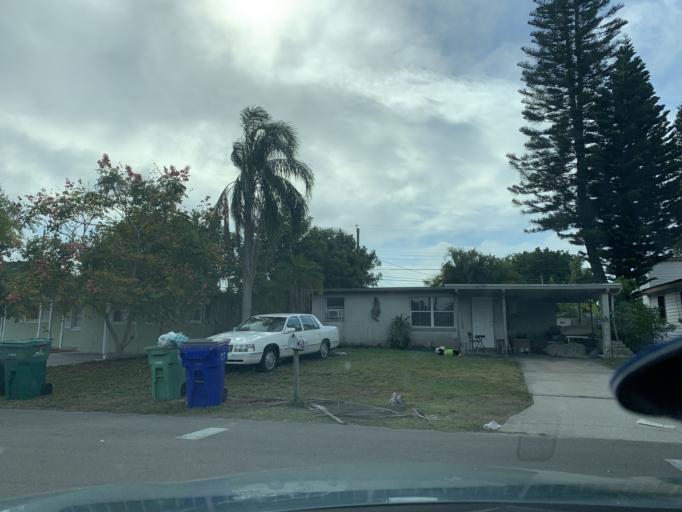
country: US
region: Florida
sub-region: Pinellas County
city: Ridgecrest
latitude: 27.8780
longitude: -82.7856
